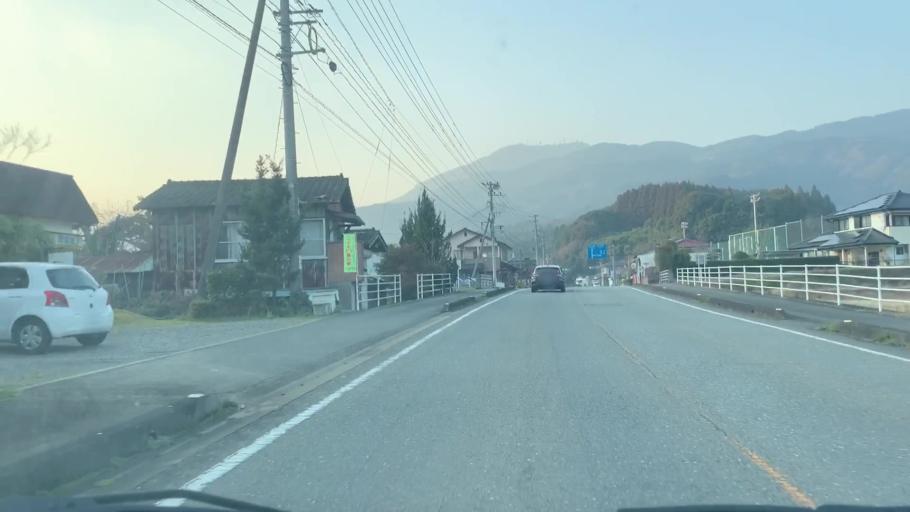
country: JP
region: Saga Prefecture
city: Takeocho-takeo
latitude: 33.2615
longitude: 130.0591
